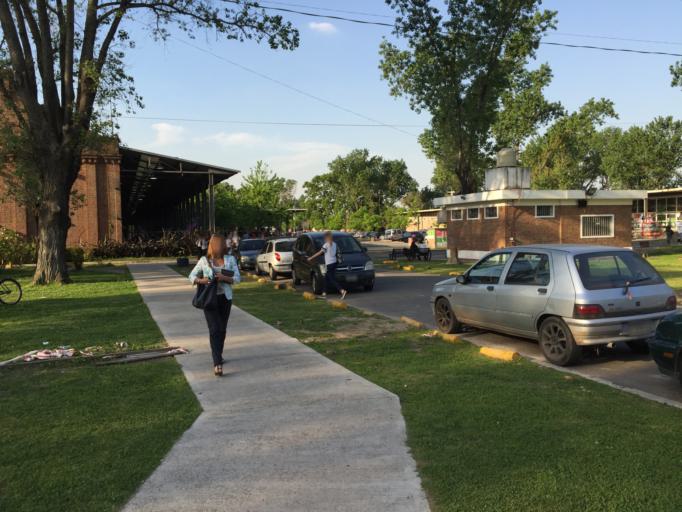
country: AR
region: Buenos Aires
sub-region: Partido de Lomas de Zamora
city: Lomas de Zamora
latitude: -34.7339
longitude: -58.3935
